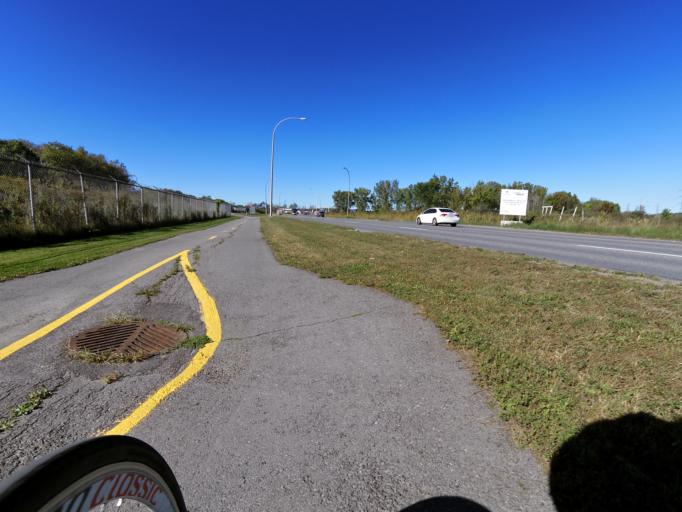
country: CA
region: Quebec
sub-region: Outaouais
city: Gatineau
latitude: 45.4833
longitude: -75.6573
